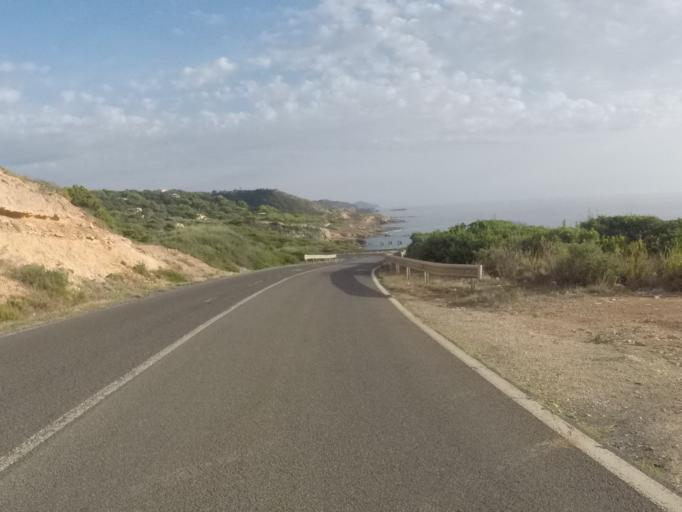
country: IT
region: Sardinia
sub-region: Provincia di Sassari
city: Alghero
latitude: 40.5269
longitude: 8.3305
